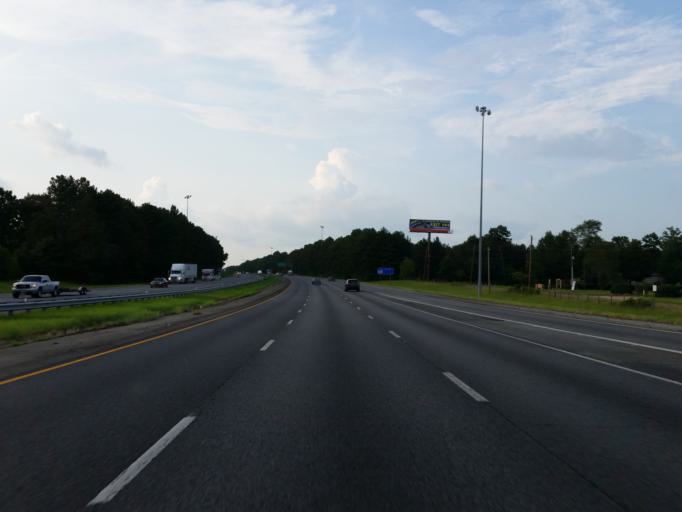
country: US
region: Georgia
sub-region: Houston County
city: Perry
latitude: 32.4747
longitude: -83.7429
